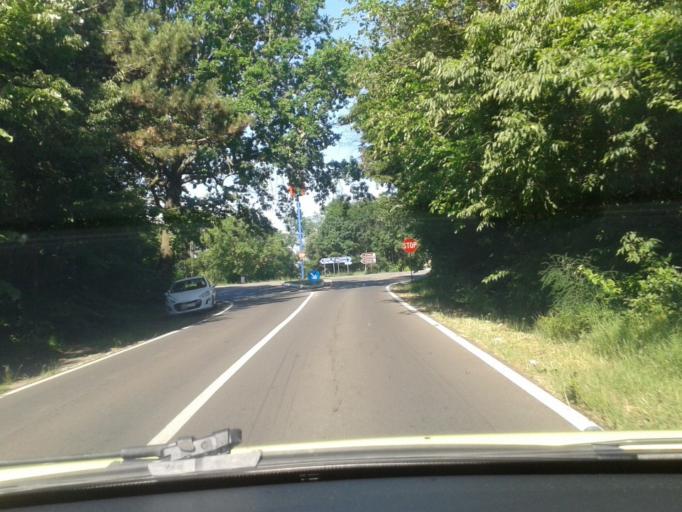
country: RO
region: Constanta
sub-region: Comuna Douazeci si Trei August
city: Dulcesti
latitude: 43.8748
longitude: 28.5753
